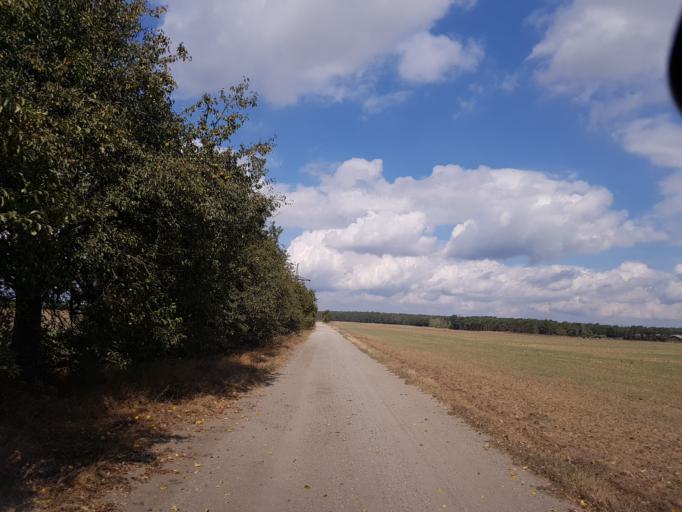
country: DE
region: Brandenburg
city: Finsterwalde
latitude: 51.6258
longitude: 13.7549
